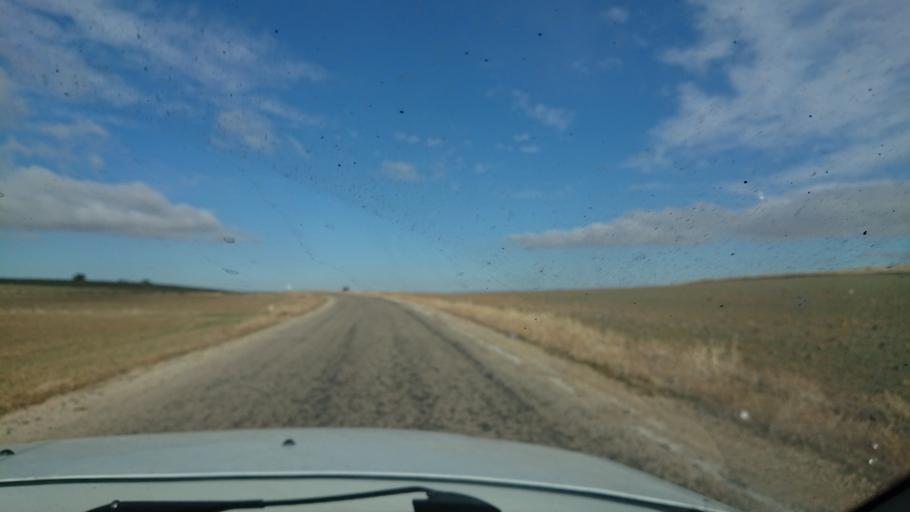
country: TR
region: Aksaray
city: Agacoren
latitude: 38.8381
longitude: 33.9537
